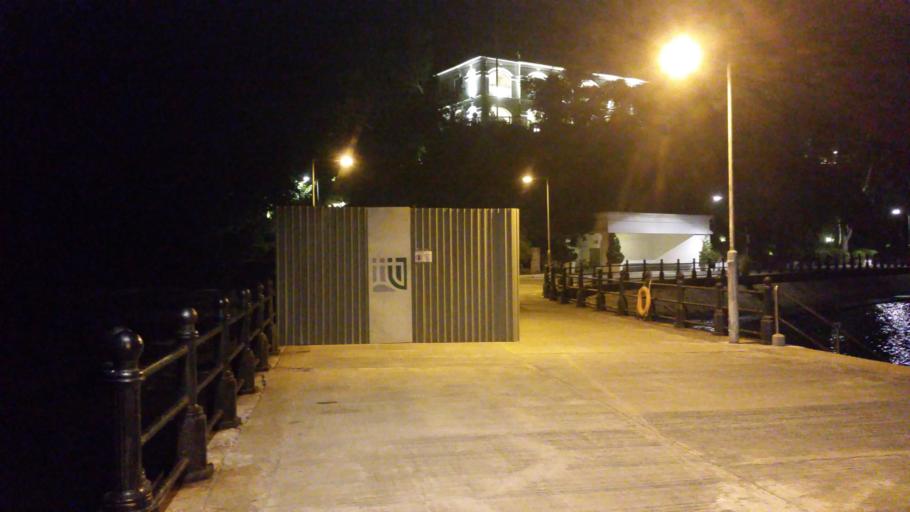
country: HK
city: Tai O
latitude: 22.2526
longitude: 113.8530
